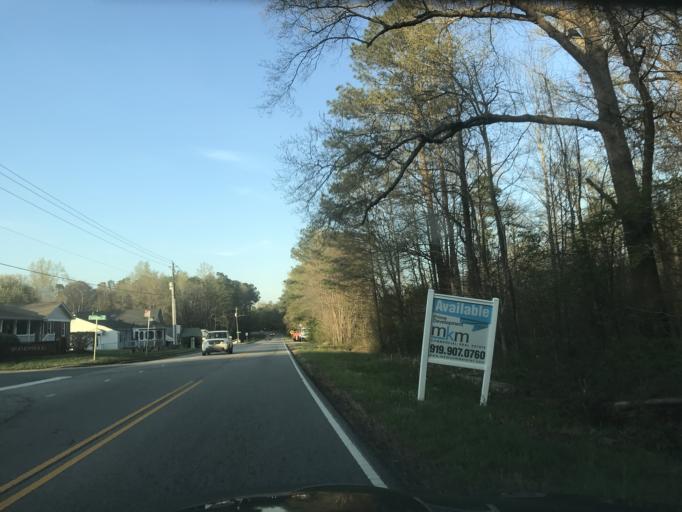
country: US
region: North Carolina
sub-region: Wake County
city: Knightdale
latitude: 35.7447
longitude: -78.5376
